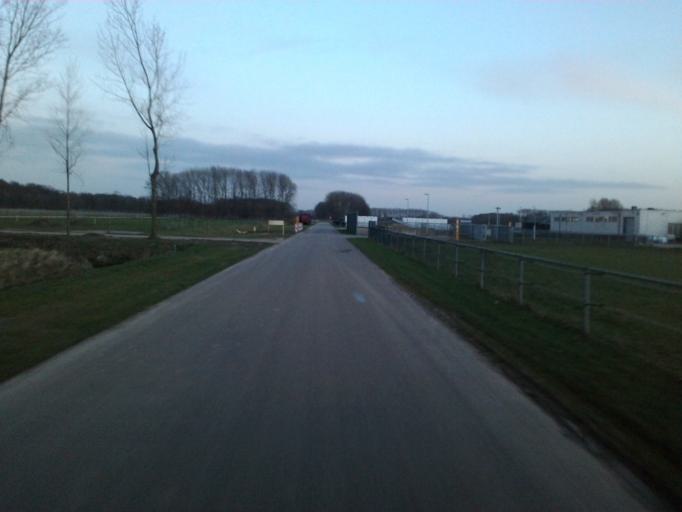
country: NL
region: Utrecht
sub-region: Gemeente De Bilt
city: De Bilt
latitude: 52.0853
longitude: 5.1819
